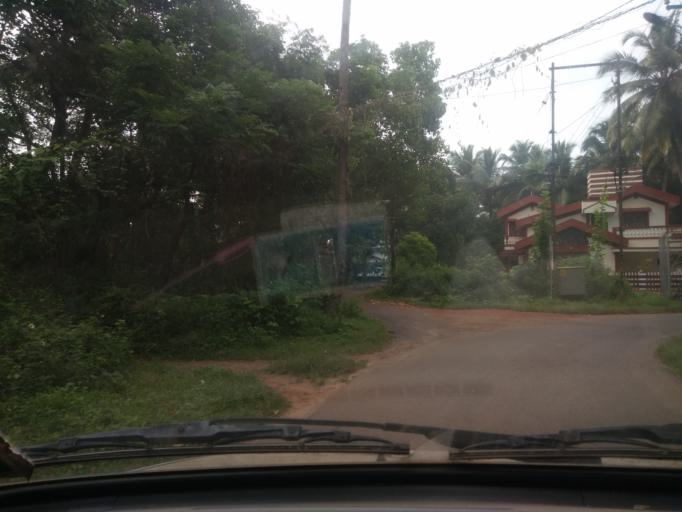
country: IN
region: Goa
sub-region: South Goa
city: Varca
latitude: 15.2157
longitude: 73.9472
